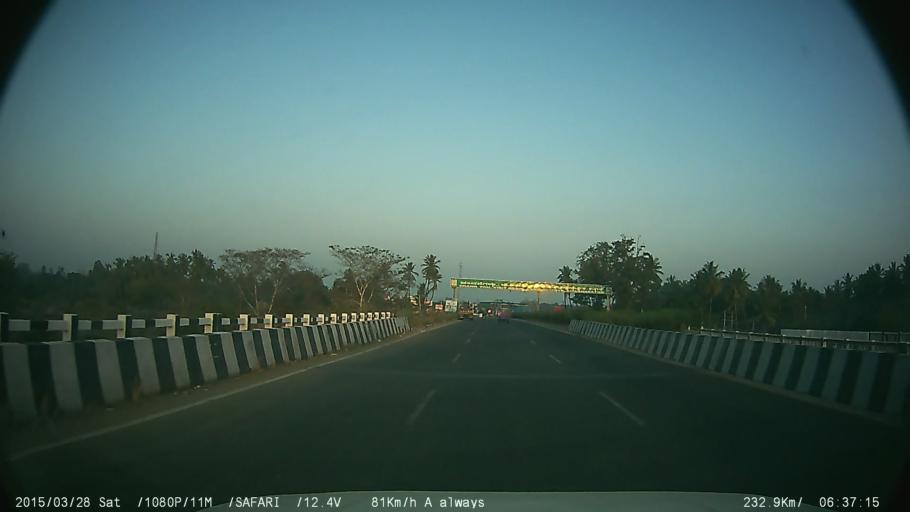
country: IN
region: Karnataka
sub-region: Ramanagara
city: Channapatna
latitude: 12.6490
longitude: 77.1854
